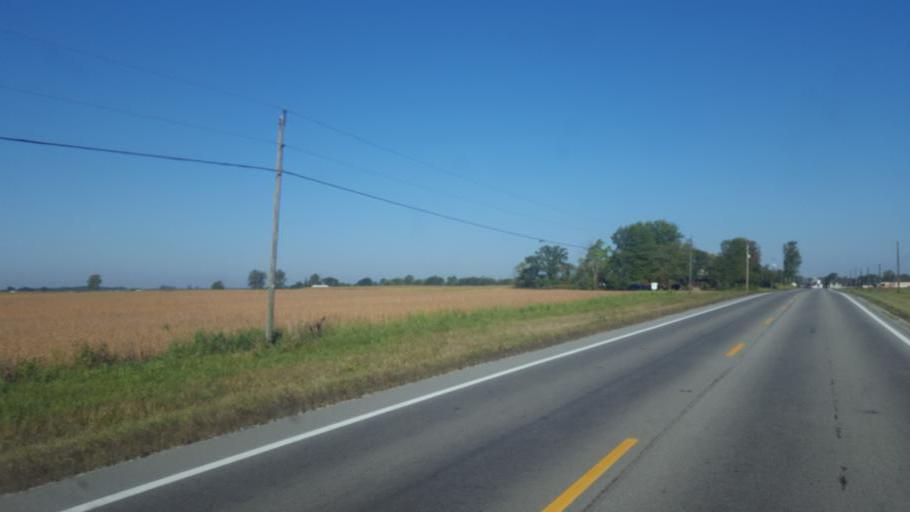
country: US
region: Ohio
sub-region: Hardin County
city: Kenton
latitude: 40.5229
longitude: -83.5123
